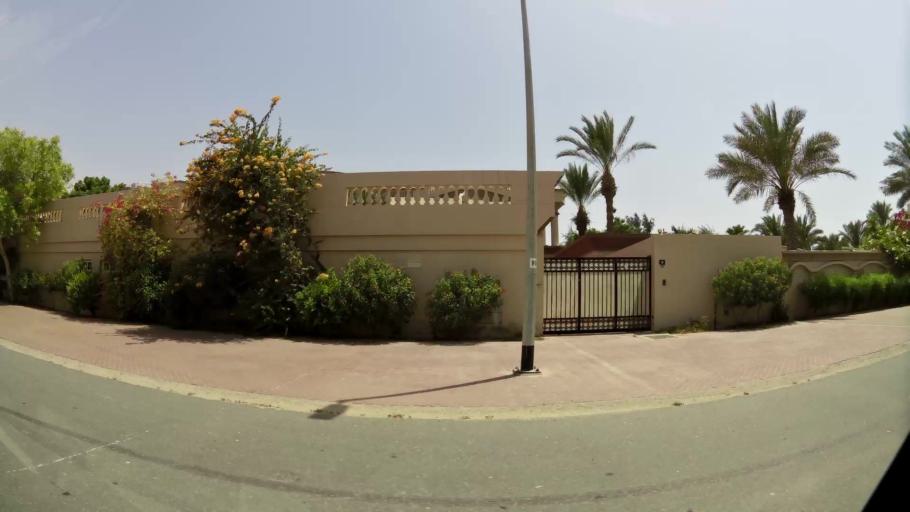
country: AE
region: Dubai
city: Dubai
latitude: 25.1317
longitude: 55.2005
